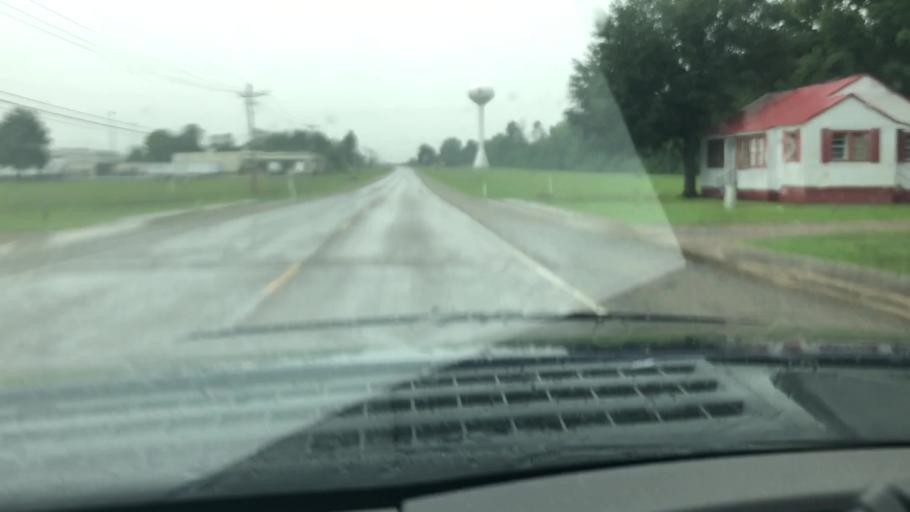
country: US
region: Texas
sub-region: Bowie County
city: Wake Village
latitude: 33.3816
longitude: -94.0932
